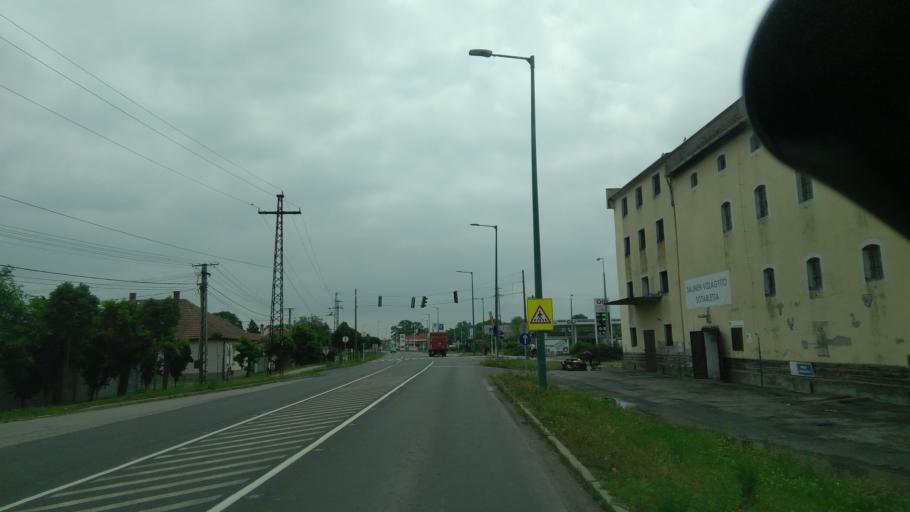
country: HU
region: Bekes
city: Gyula
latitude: 46.6426
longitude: 21.2596
